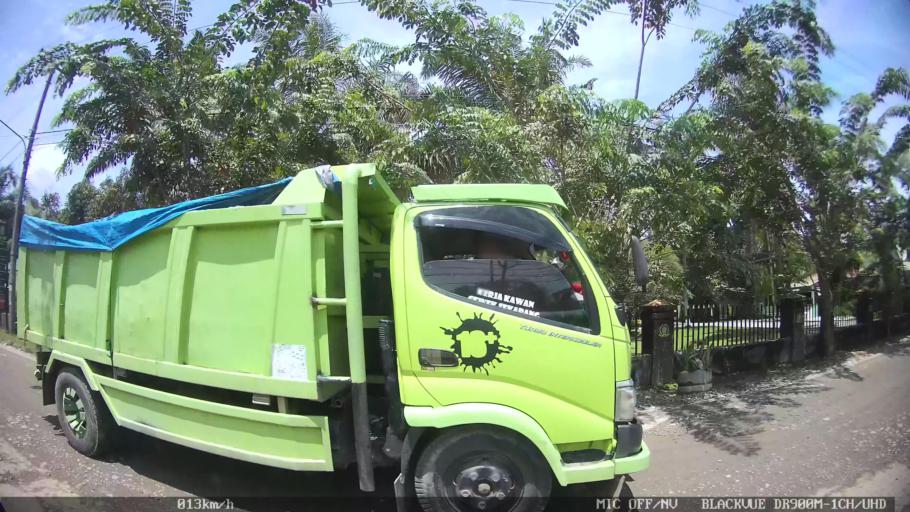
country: ID
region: North Sumatra
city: Perbaungan
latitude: 3.5405
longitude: 98.8825
